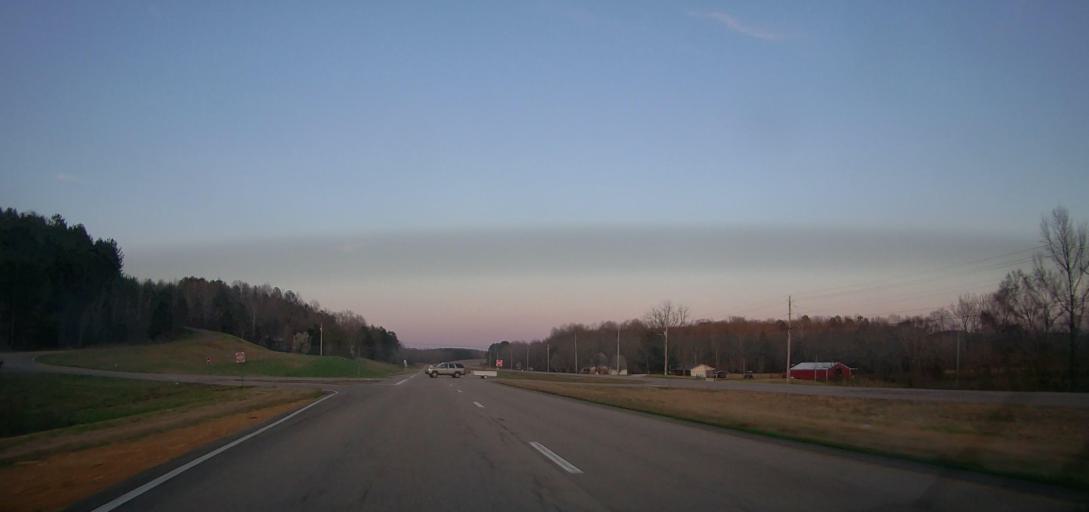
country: US
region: Mississippi
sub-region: Alcorn County
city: Corinth
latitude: 34.9345
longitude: -88.7477
